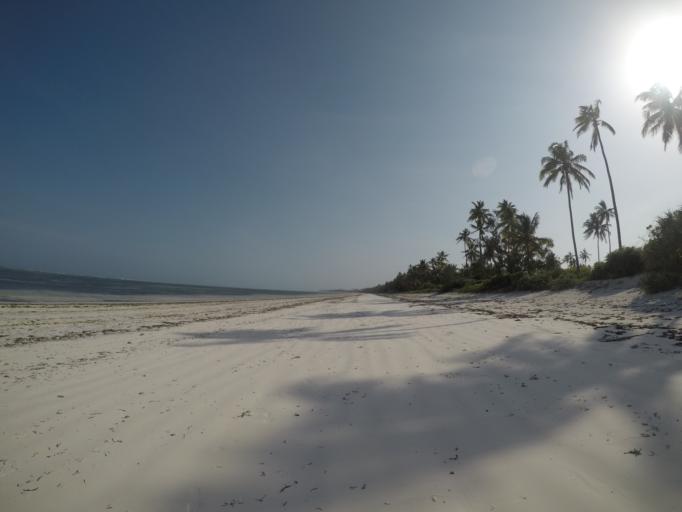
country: TZ
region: Zanzibar Central/South
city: Nganane
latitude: -6.2118
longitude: 39.5342
